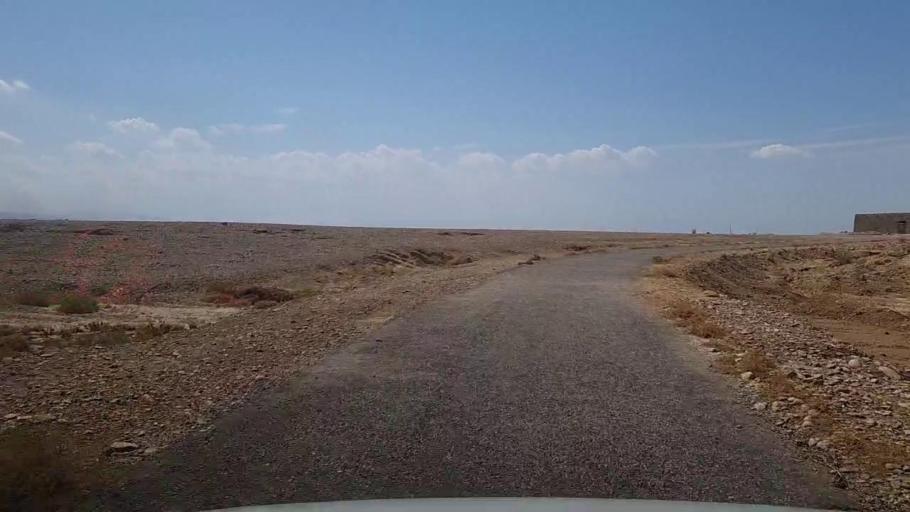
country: PK
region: Sindh
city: Bhan
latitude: 26.3815
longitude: 67.6294
